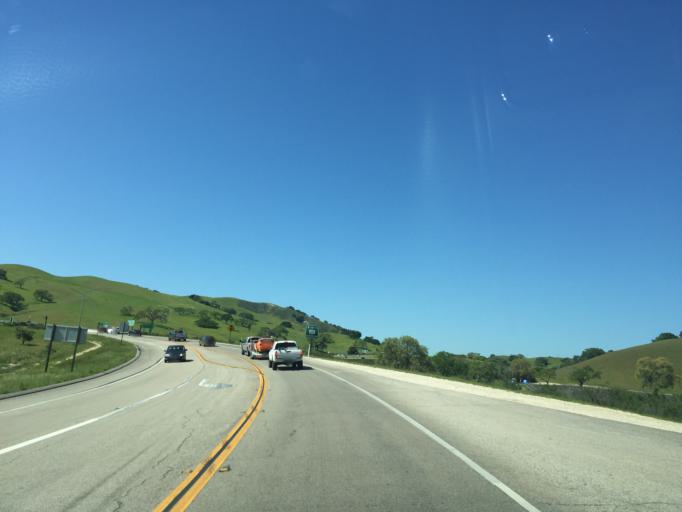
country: US
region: California
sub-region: Santa Barbara County
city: Los Olivos
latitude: 34.6871
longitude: -120.1555
